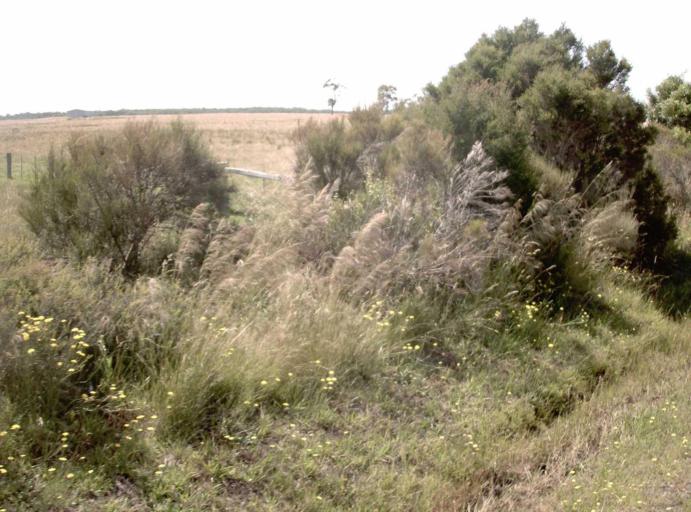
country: AU
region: Victoria
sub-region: Bass Coast
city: North Wonthaggi
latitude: -38.5822
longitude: 145.7209
